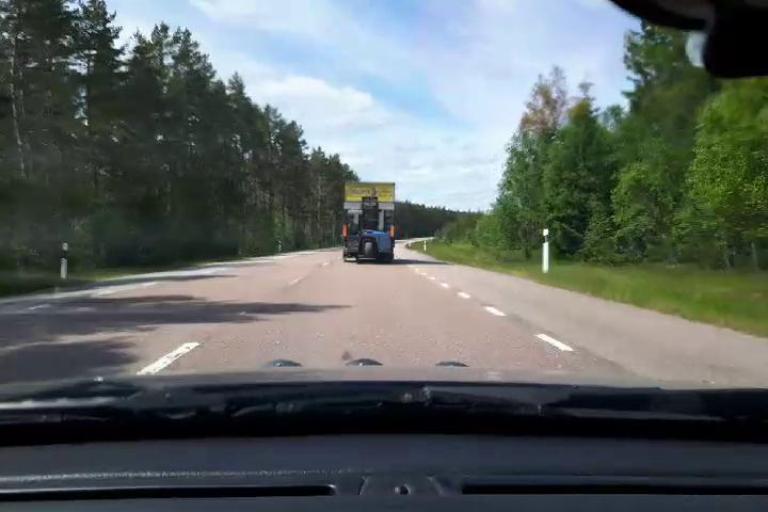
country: SE
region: Uppsala
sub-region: Osthammars Kommun
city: Bjorklinge
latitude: 60.1119
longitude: 17.5280
